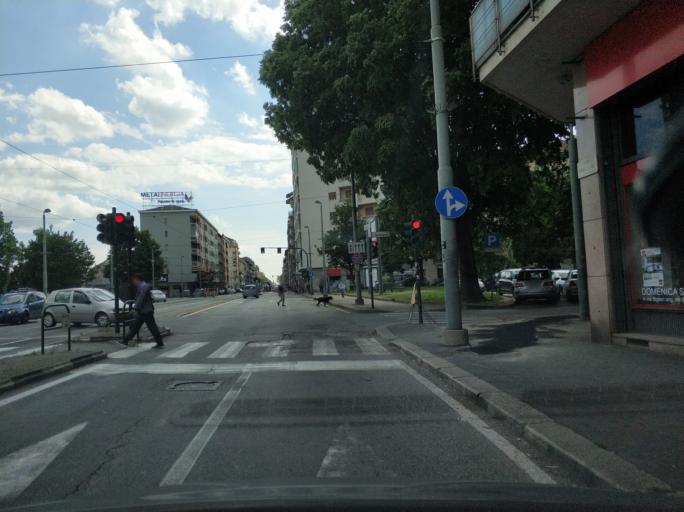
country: IT
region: Piedmont
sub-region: Provincia di Torino
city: Turin
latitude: 45.0996
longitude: 7.6984
